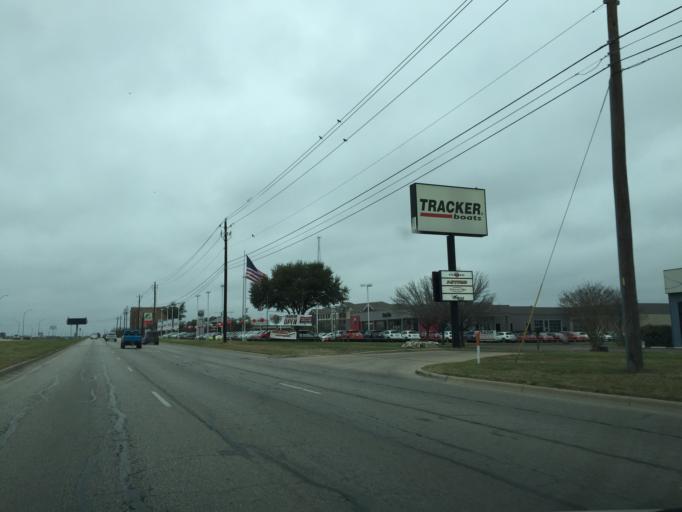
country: US
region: Texas
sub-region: Williamson County
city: Jollyville
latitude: 30.4386
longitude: -97.7772
